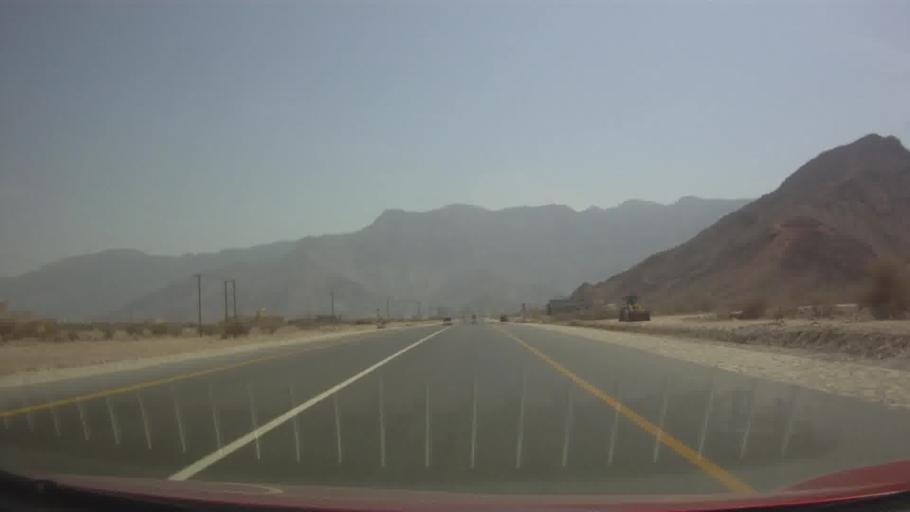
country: OM
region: Muhafazat Masqat
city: Muscat
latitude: 23.4206
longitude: 58.7814
